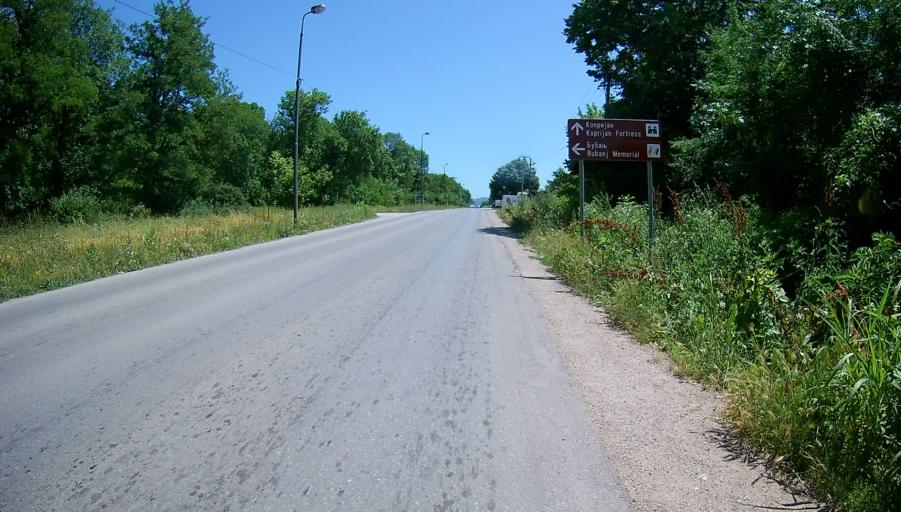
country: RS
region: Central Serbia
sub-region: Nisavski Okrug
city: Nis
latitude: 43.3035
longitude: 21.8701
